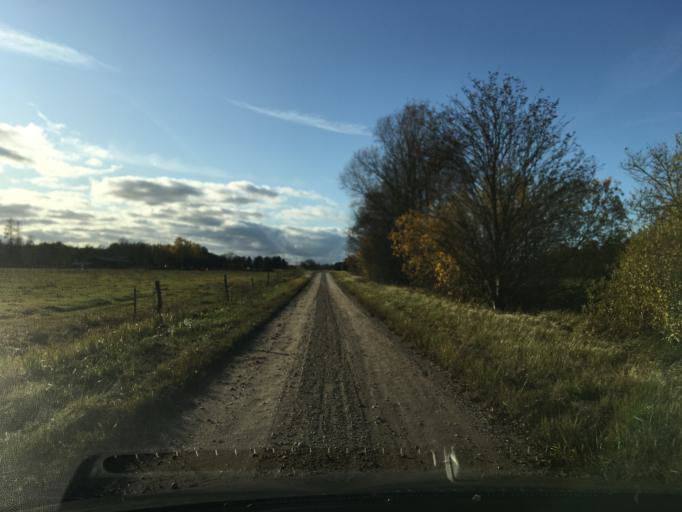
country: EE
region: Laeaene
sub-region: Lihula vald
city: Lihula
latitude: 58.5636
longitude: 23.8062
